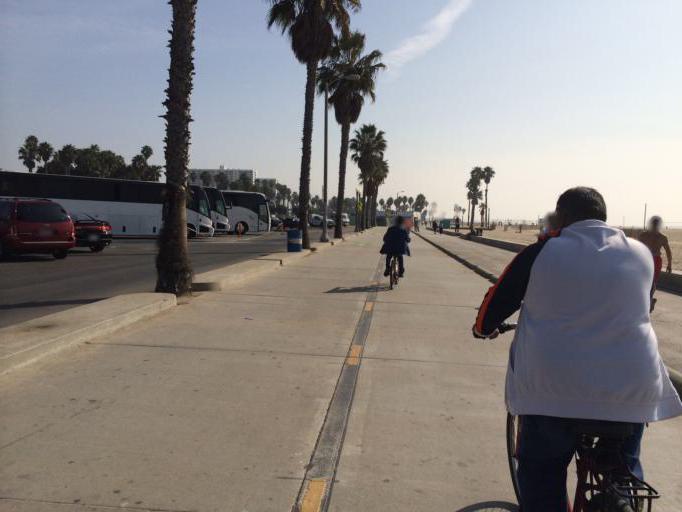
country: US
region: California
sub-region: Los Angeles County
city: Santa Monica
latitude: 34.0036
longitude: -118.4897
